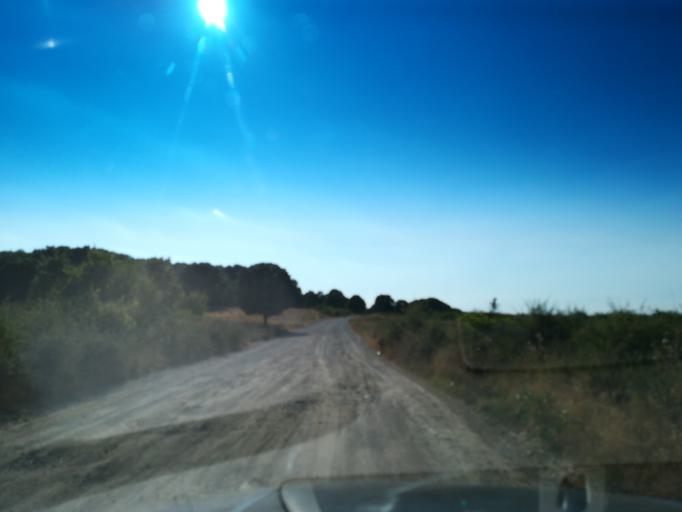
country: BG
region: Khaskovo
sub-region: Obshtina Mineralni Bani
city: Mineralni Bani
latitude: 41.9715
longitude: 25.3388
